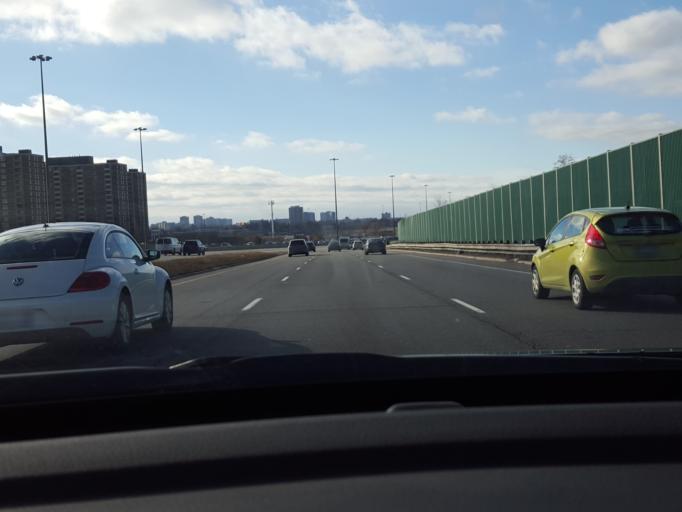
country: CA
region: Ontario
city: Concord
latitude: 43.7193
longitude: -79.5004
